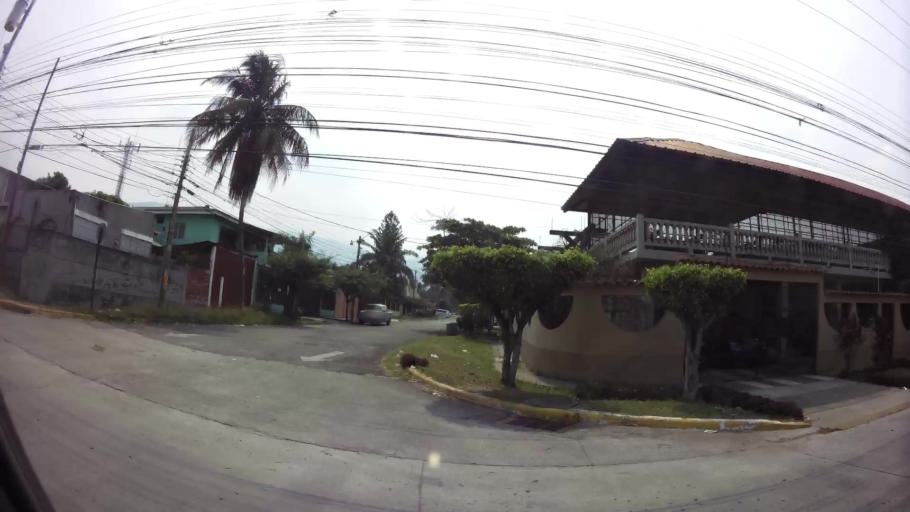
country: HN
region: Cortes
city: San Pedro Sula
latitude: 15.4870
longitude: -88.0330
